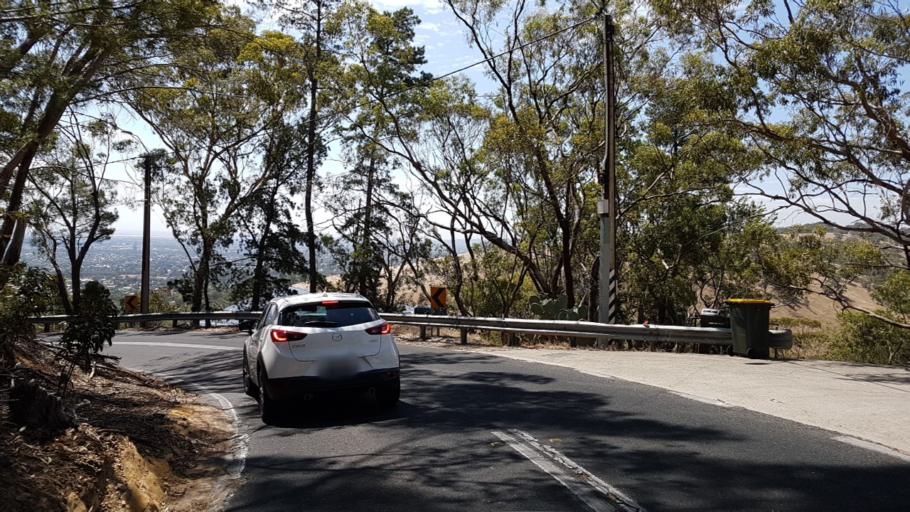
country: AU
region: South Australia
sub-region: Mitcham
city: Belair
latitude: -34.9954
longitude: 138.6298
